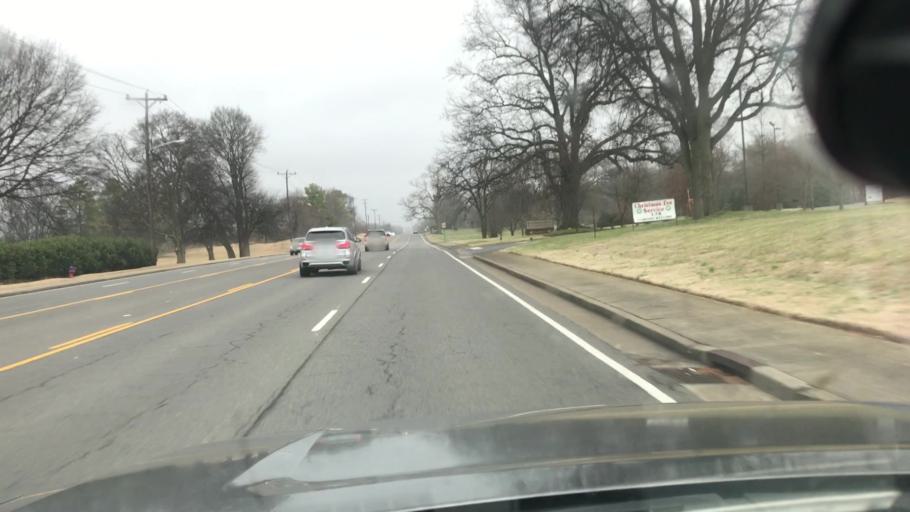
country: US
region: Tennessee
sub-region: Williamson County
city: Brentwood Estates
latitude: 36.0188
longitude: -86.7968
